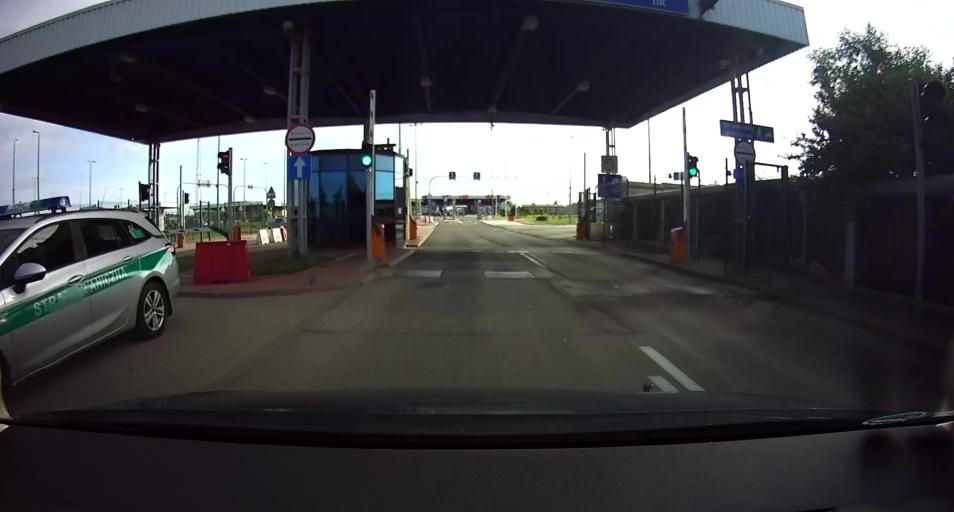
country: PL
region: Podlasie
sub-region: Powiat sokolski
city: Kuznica
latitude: 53.5194
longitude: 23.6550
